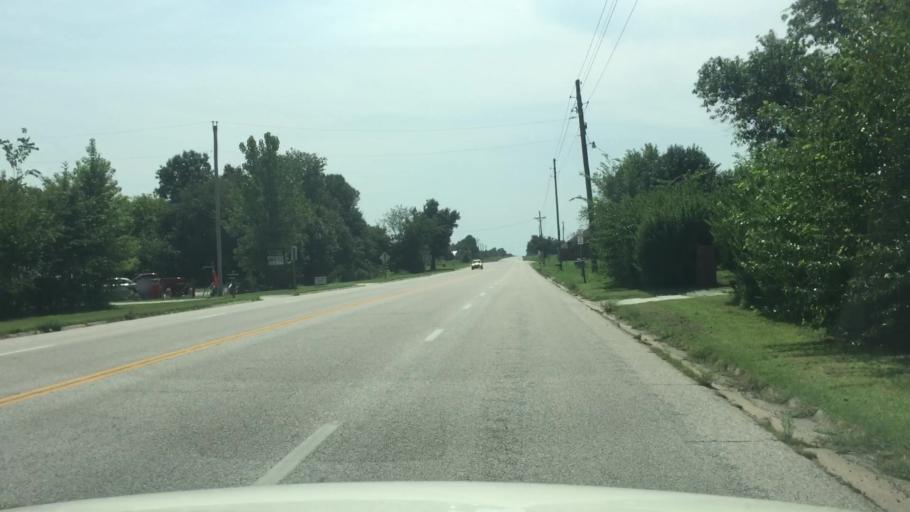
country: US
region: Kansas
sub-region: Cherokee County
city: Galena
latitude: 37.1654
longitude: -94.7044
